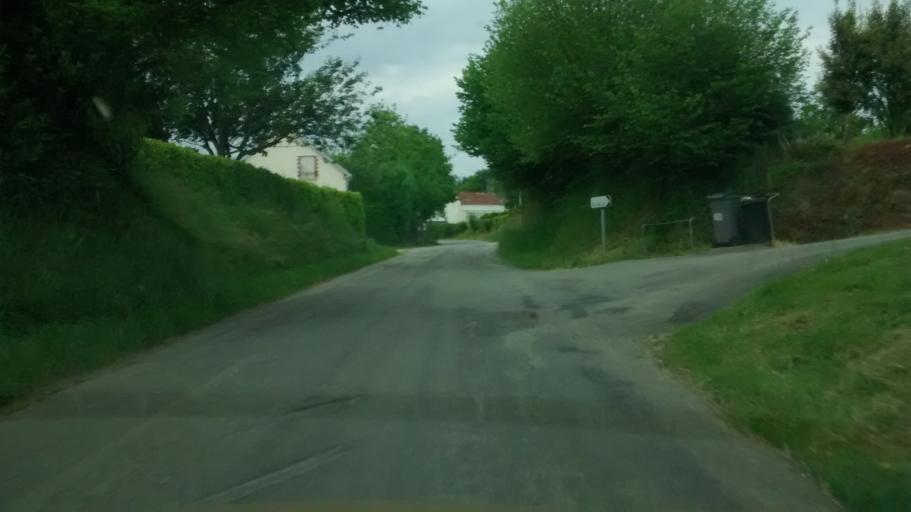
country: FR
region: Brittany
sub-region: Departement du Morbihan
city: Molac
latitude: 47.7218
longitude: -2.4295
